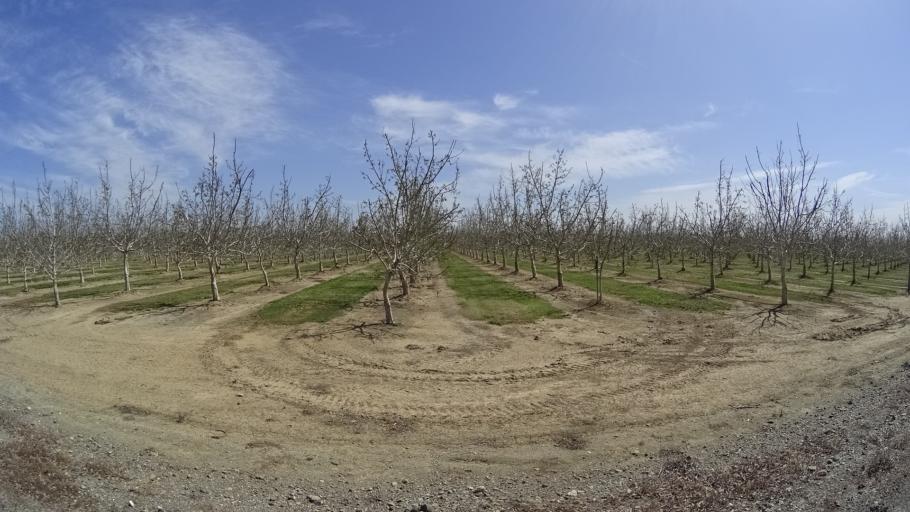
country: US
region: California
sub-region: Glenn County
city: Hamilton City
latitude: 39.6399
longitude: -122.0743
